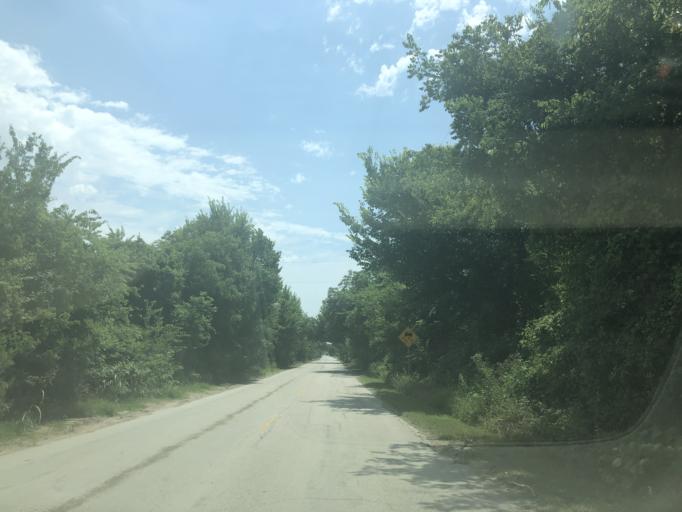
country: US
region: Texas
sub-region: Dallas County
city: Irving
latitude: 32.7867
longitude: -96.9541
